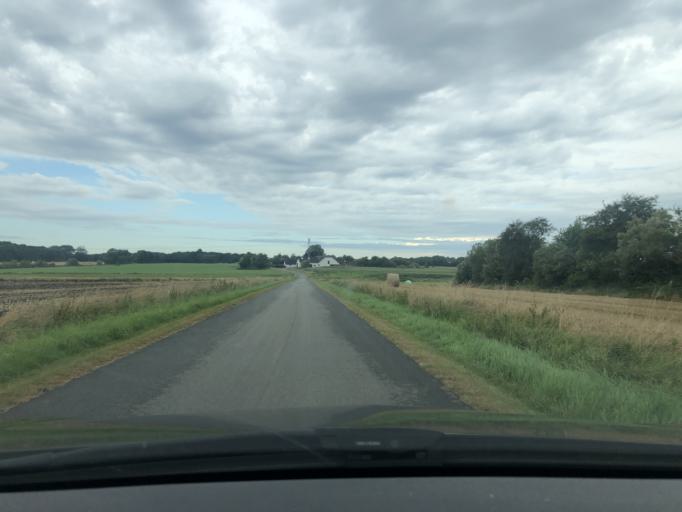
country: DK
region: South Denmark
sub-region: Varde Kommune
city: Olgod
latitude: 55.8075
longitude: 8.6916
